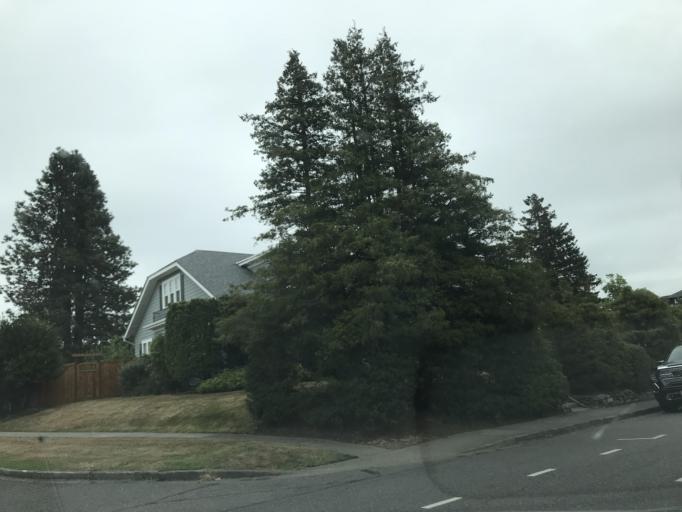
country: US
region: Washington
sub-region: Whatcom County
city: Bellingham
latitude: 48.7665
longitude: -122.4764
